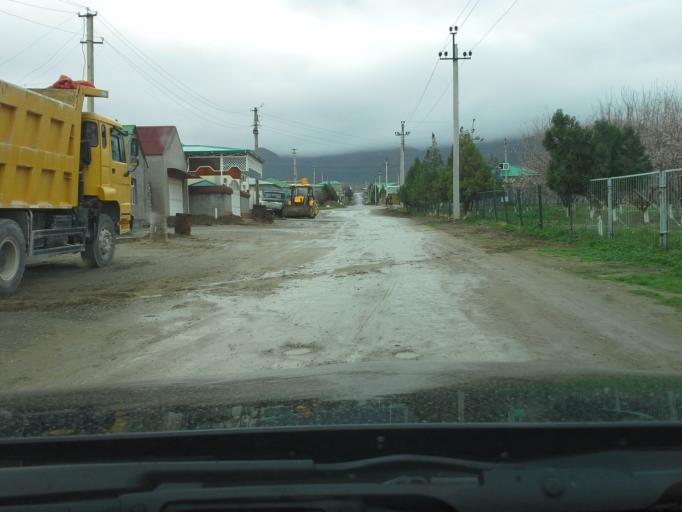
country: TM
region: Ahal
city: Abadan
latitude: 37.9647
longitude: 58.2064
